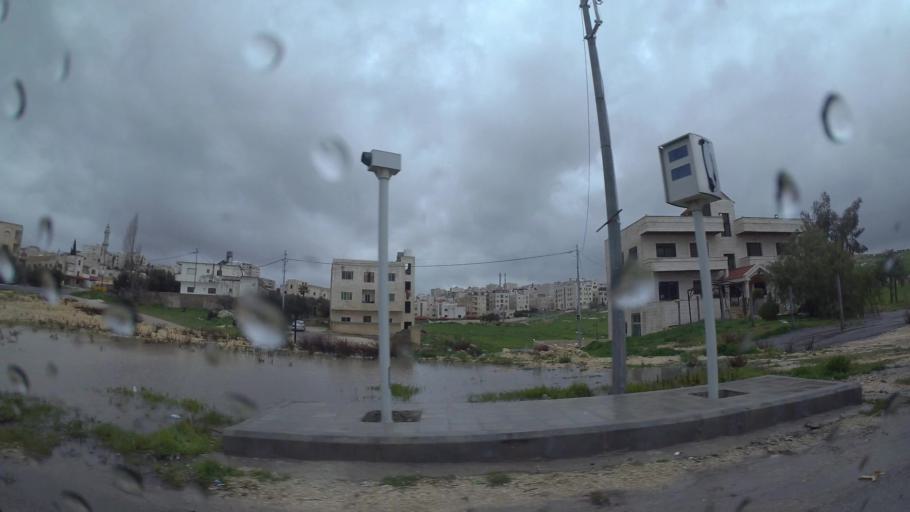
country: JO
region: Amman
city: Al Jubayhah
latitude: 32.0384
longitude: 35.8967
